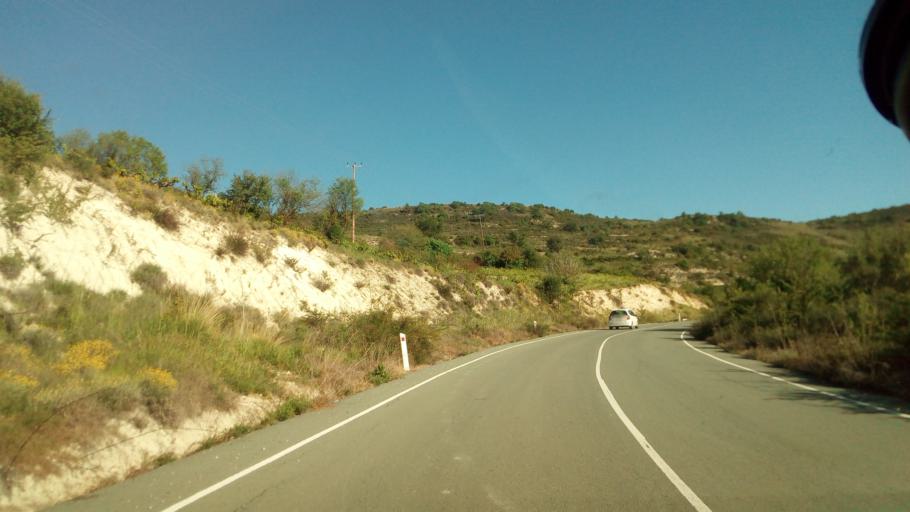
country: CY
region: Limassol
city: Pachna
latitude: 34.8628
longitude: 32.7596
